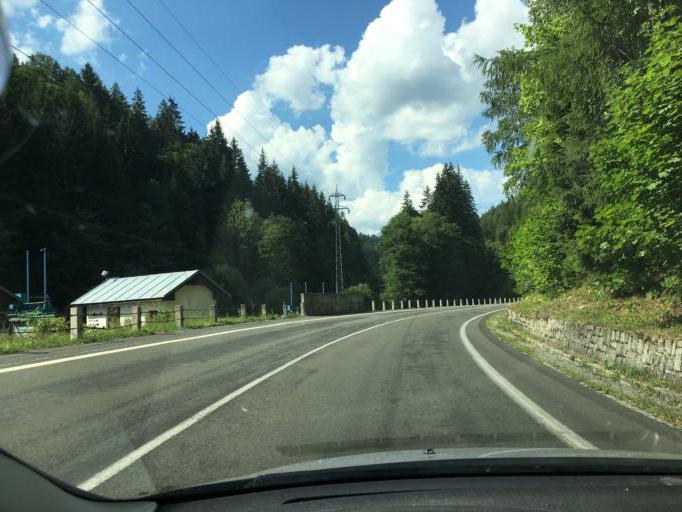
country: CZ
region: Kralovehradecky
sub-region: Okres Trutnov
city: Vrchlabi
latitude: 50.6642
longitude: 15.5940
